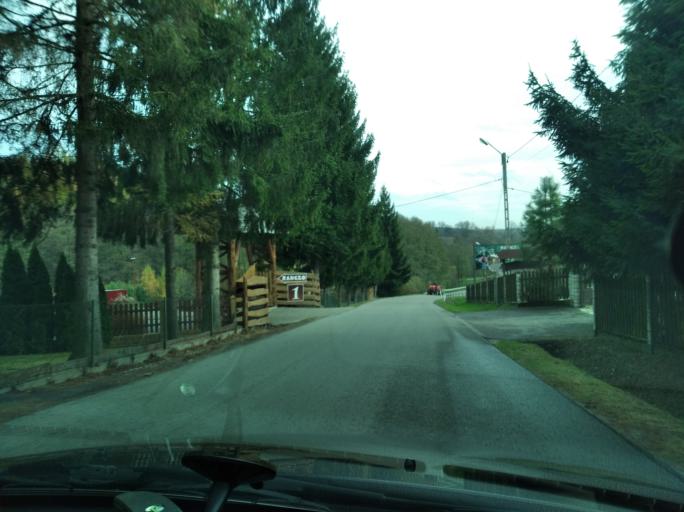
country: PL
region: Subcarpathian Voivodeship
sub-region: Powiat ropczycko-sedziszowski
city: Zagorzyce
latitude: 49.9550
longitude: 21.7198
